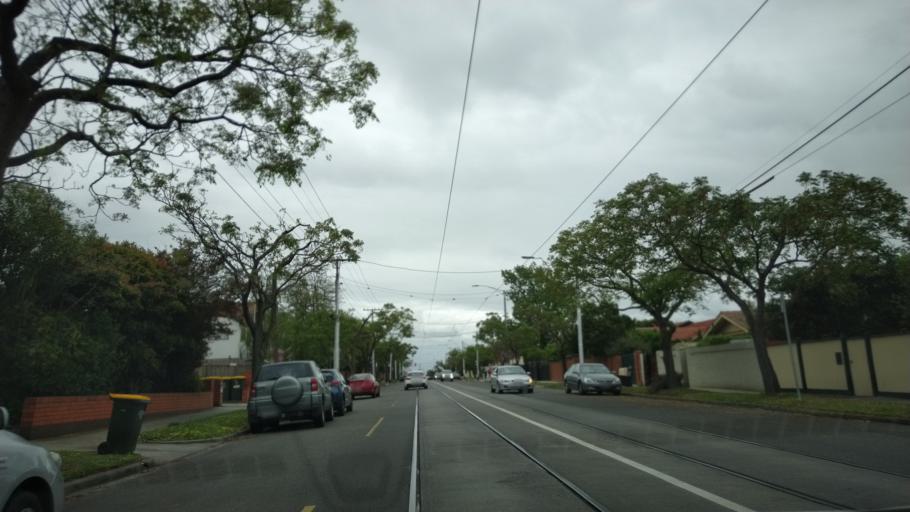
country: AU
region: Victoria
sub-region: Glen Eira
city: Caulfield South
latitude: -37.8884
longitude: 145.0342
